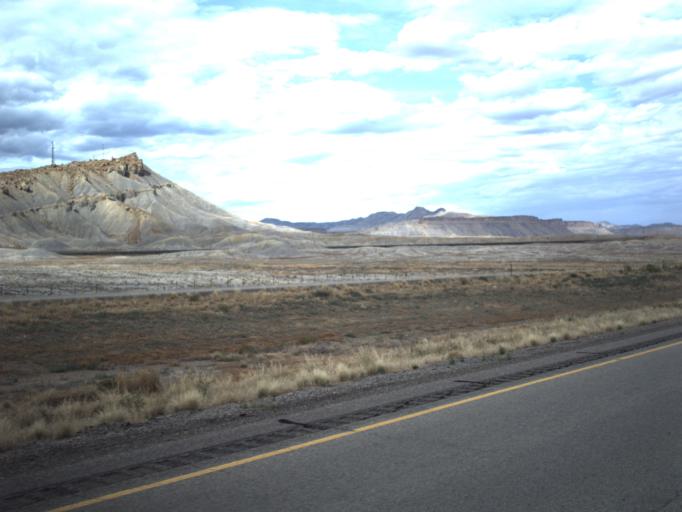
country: US
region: Utah
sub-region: Grand County
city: Moab
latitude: 38.9313
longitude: -109.8677
